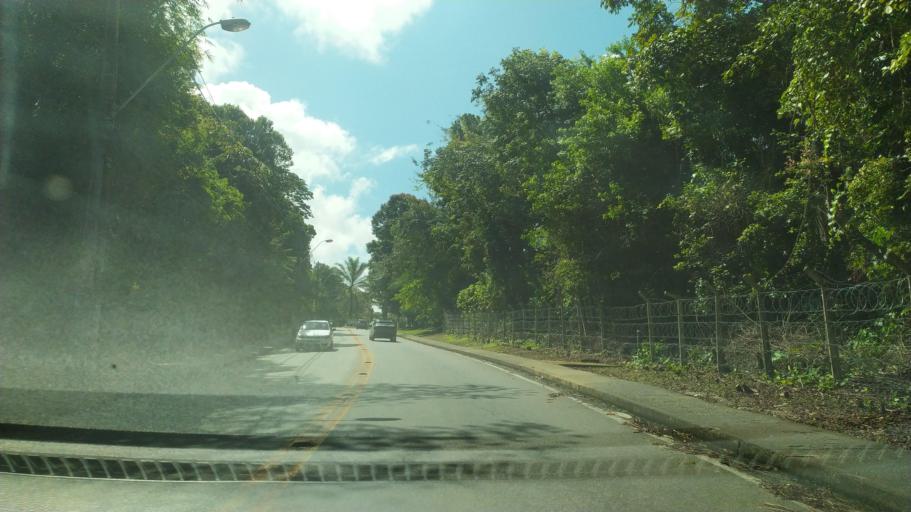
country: BR
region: Alagoas
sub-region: Maceio
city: Maceio
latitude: -9.5956
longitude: -35.7376
